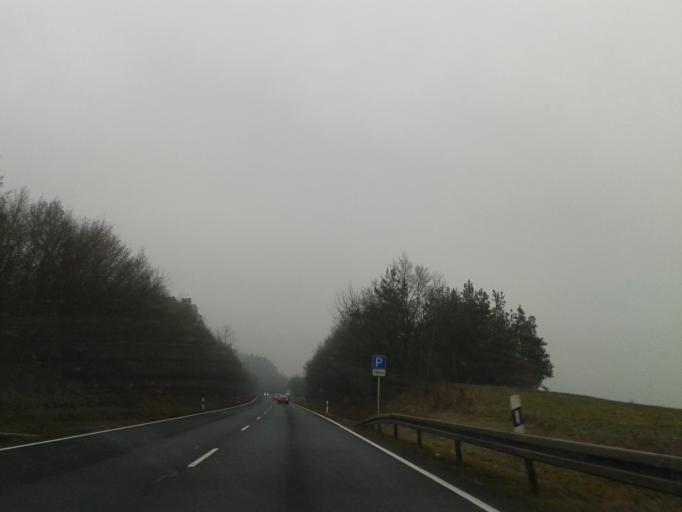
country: DE
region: Bavaria
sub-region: Regierungsbezirk Unterfranken
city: Burgpreppach
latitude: 50.1502
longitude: 10.6692
